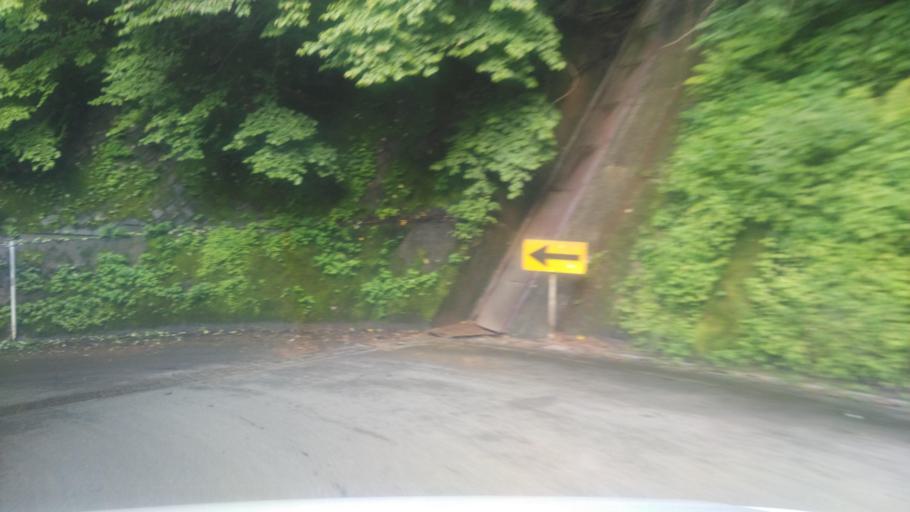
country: JP
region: Nagano
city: Suzaka
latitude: 36.5445
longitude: 138.2993
